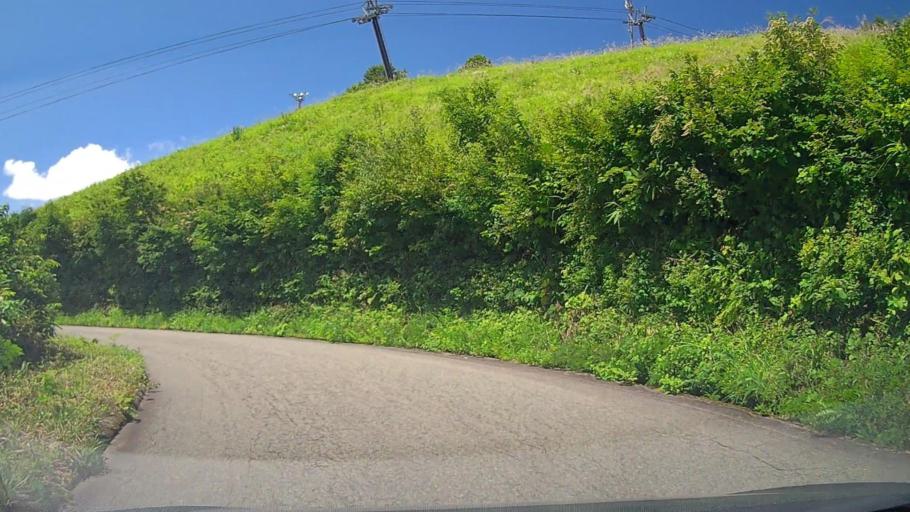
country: JP
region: Nagano
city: Iiyama
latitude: 36.9343
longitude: 138.4566
